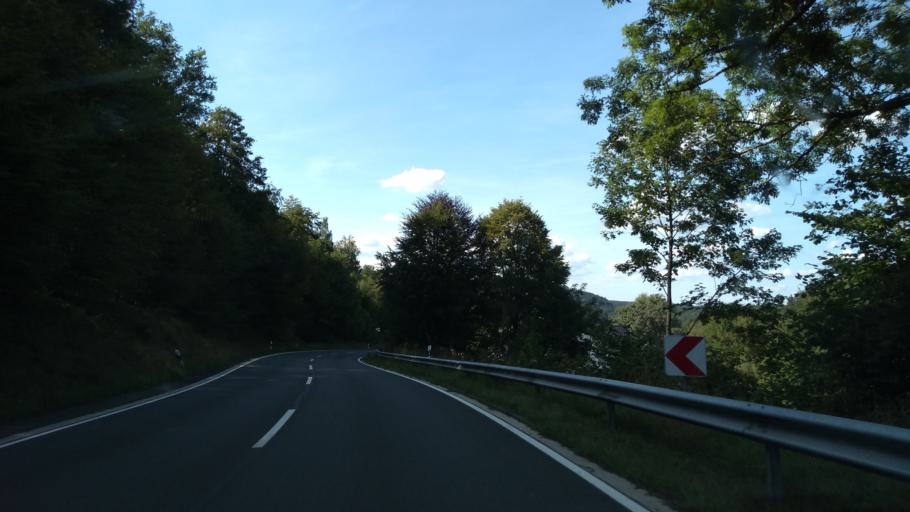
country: DE
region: North Rhine-Westphalia
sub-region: Regierungsbezirk Arnsberg
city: Olpe
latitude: 51.0596
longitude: 7.8550
